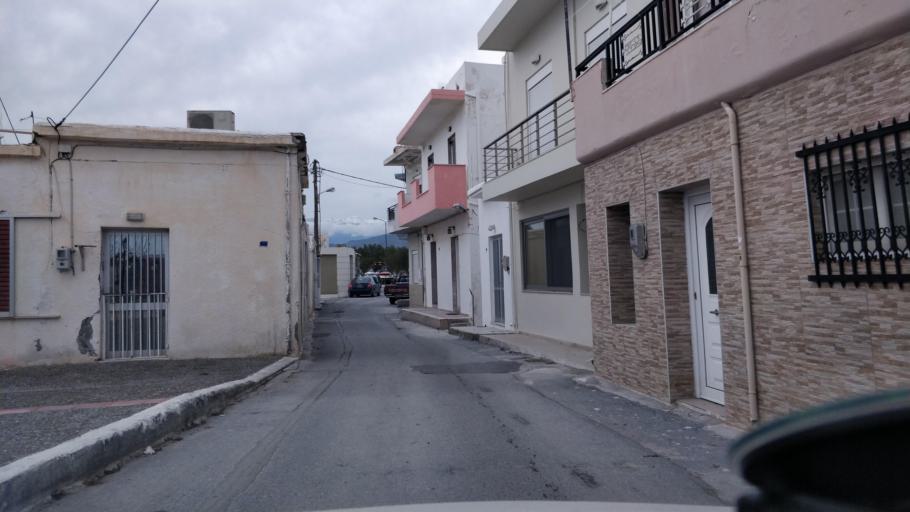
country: GR
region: Crete
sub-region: Nomos Lasithiou
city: Ierapetra
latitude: 35.0041
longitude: 25.7361
